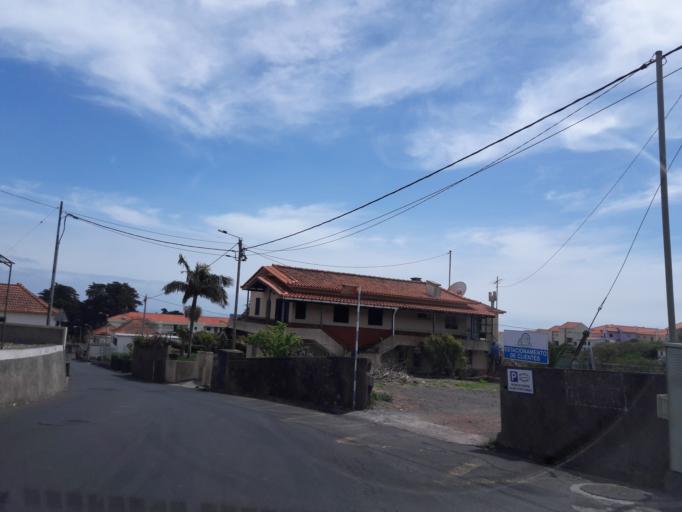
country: PT
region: Madeira
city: Canico
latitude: 32.6513
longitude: -16.8539
